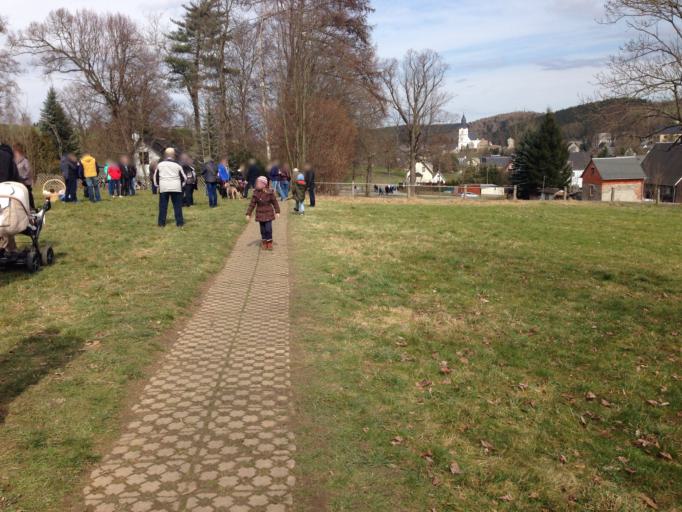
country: DE
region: Saxony
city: Venusberg
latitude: 50.6839
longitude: 13.0226
